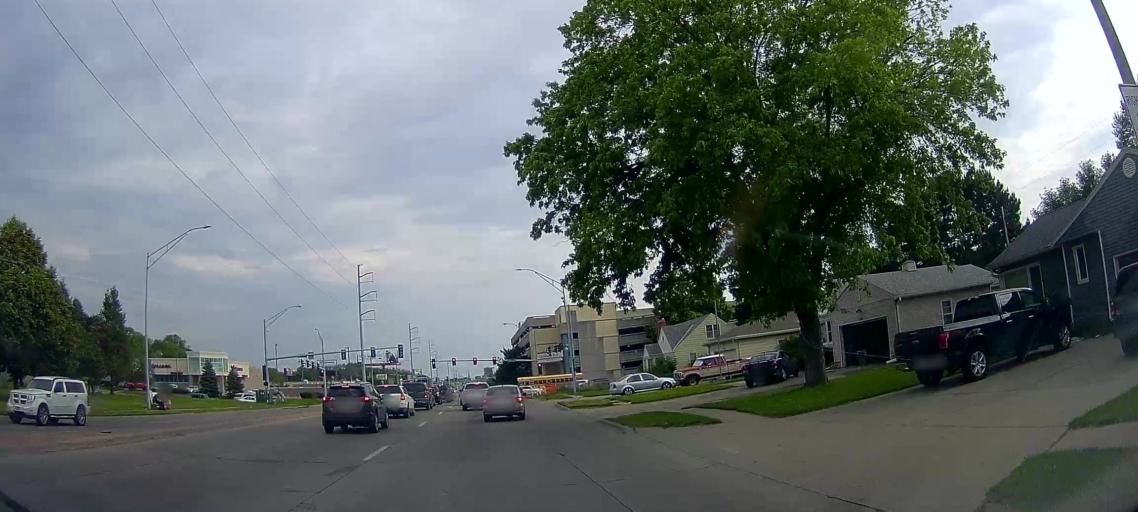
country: US
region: Nebraska
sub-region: Douglas County
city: Ralston
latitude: 41.2641
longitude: -96.0240
